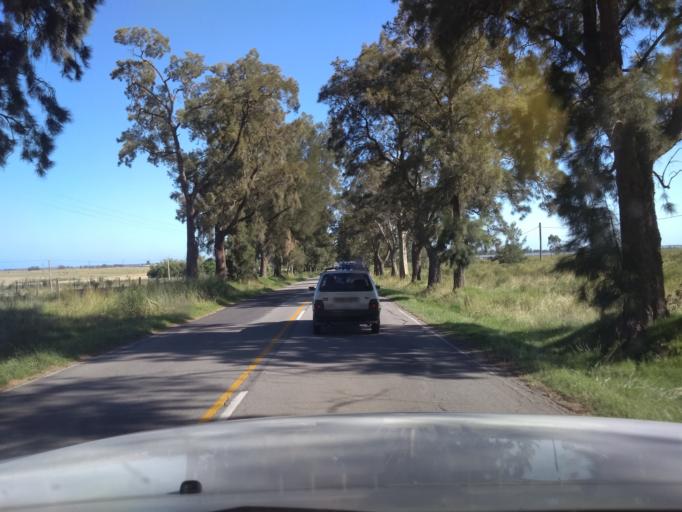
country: UY
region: Canelones
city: San Bautista
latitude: -34.3953
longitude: -55.9596
